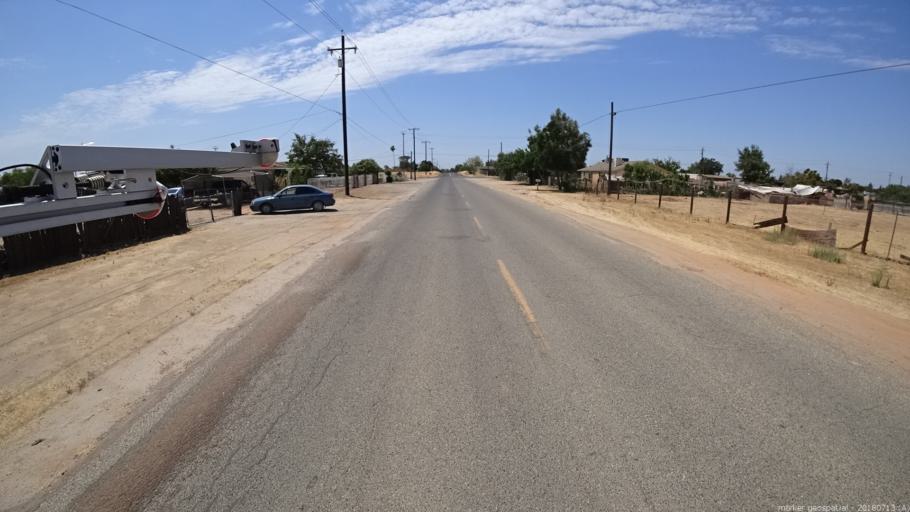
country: US
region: California
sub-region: Madera County
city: Madera
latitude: 36.9838
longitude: -120.0596
